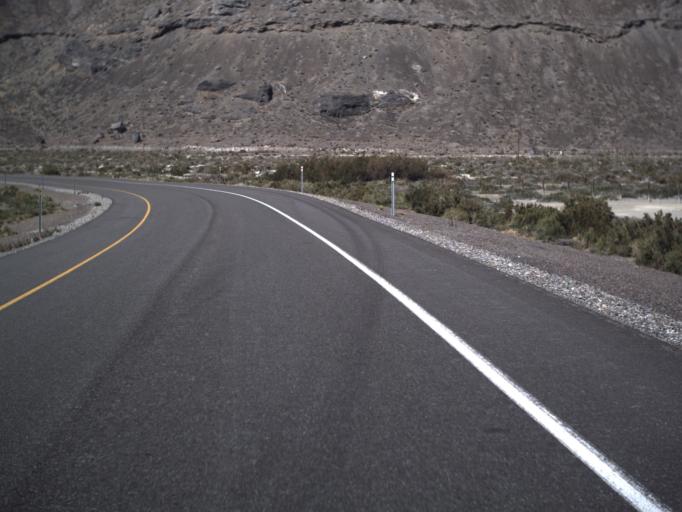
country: US
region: Utah
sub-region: Tooele County
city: Wendover
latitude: 40.7491
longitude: -114.0106
